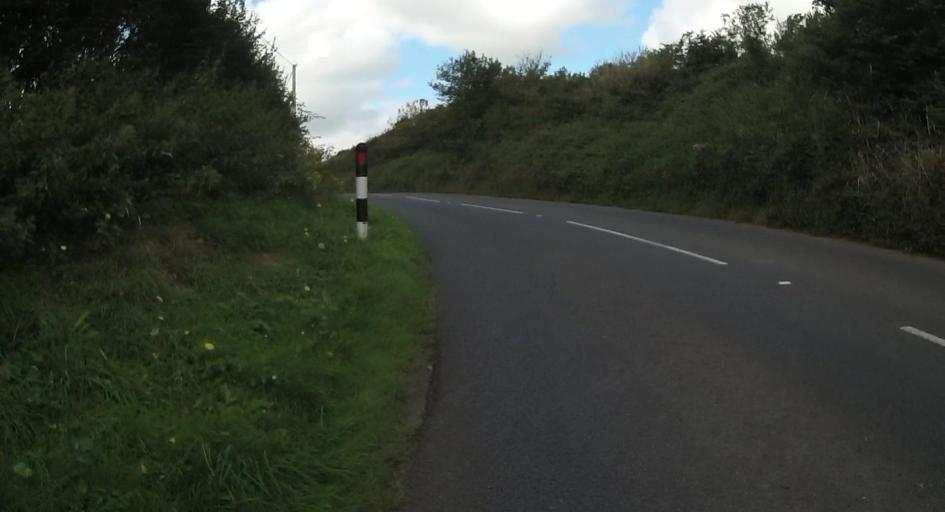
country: GB
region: England
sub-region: Isle of Wight
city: Shalfleet
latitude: 50.6475
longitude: -1.4095
